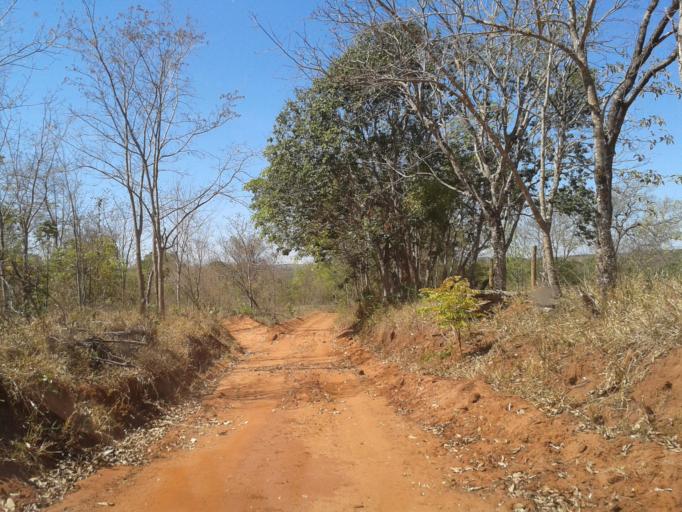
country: BR
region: Minas Gerais
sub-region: Ituiutaba
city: Ituiutaba
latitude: -19.0990
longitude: -49.2998
